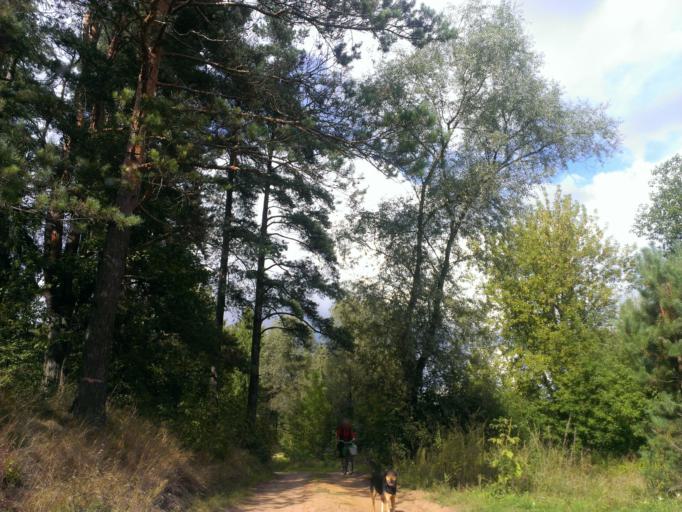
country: LV
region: Garkalne
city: Garkalne
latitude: 56.9716
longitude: 24.4849
